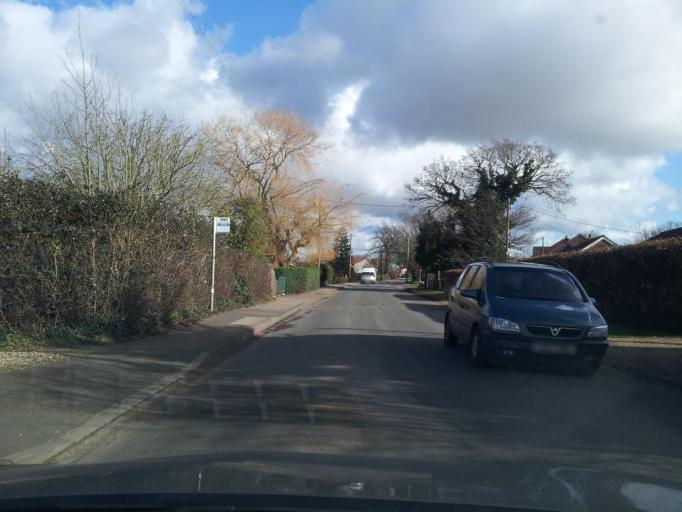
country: GB
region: England
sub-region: Norfolk
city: Mattishall
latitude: 52.6606
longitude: 1.0186
